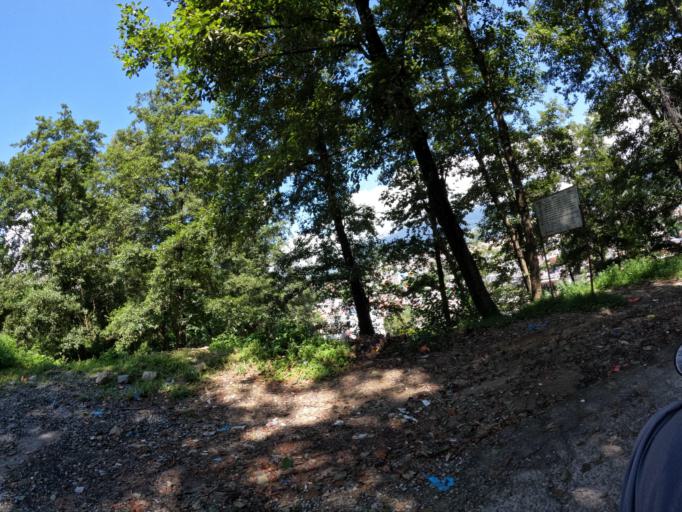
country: NP
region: Central Region
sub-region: Bagmati Zone
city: Kathmandu
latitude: 27.7541
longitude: 85.3317
